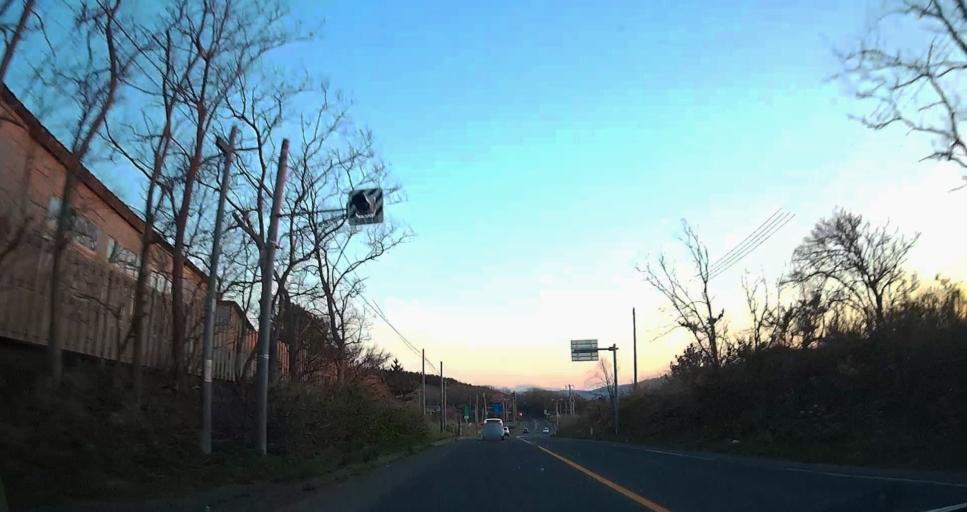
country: JP
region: Aomori
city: Misawa
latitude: 40.8867
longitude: 141.1601
